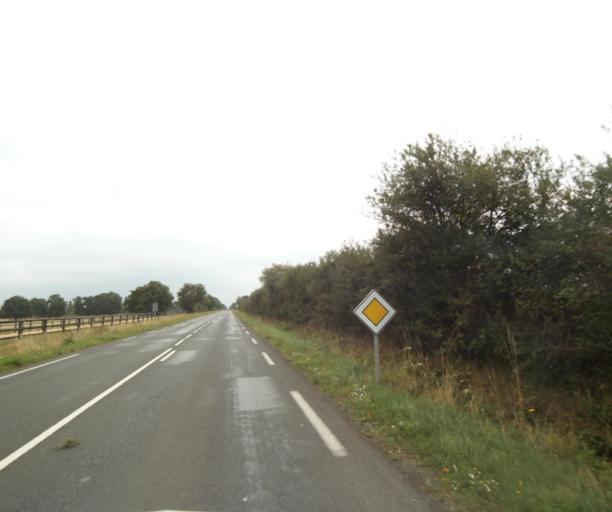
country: FR
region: Pays de la Loire
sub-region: Departement de la Sarthe
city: Solesmes
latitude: 47.8381
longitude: -0.2864
